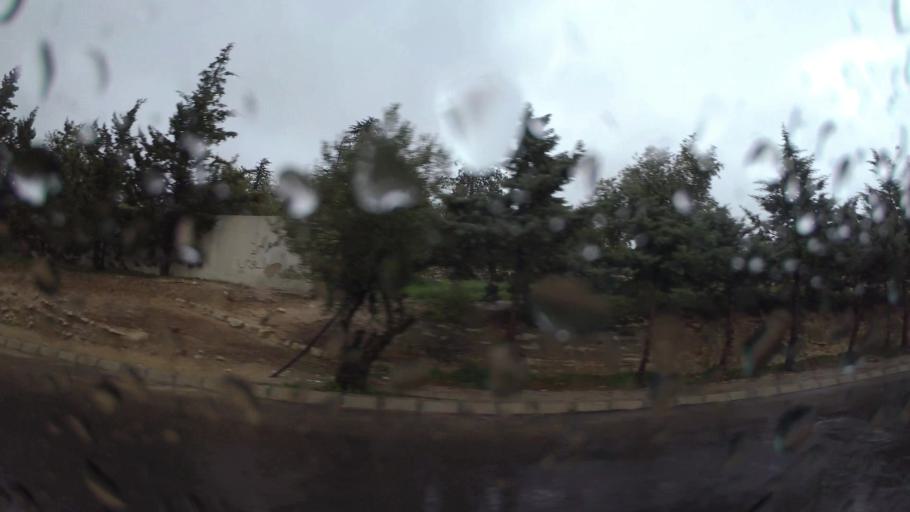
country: JO
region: Amman
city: Al Jubayhah
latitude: 32.0255
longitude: 35.8605
